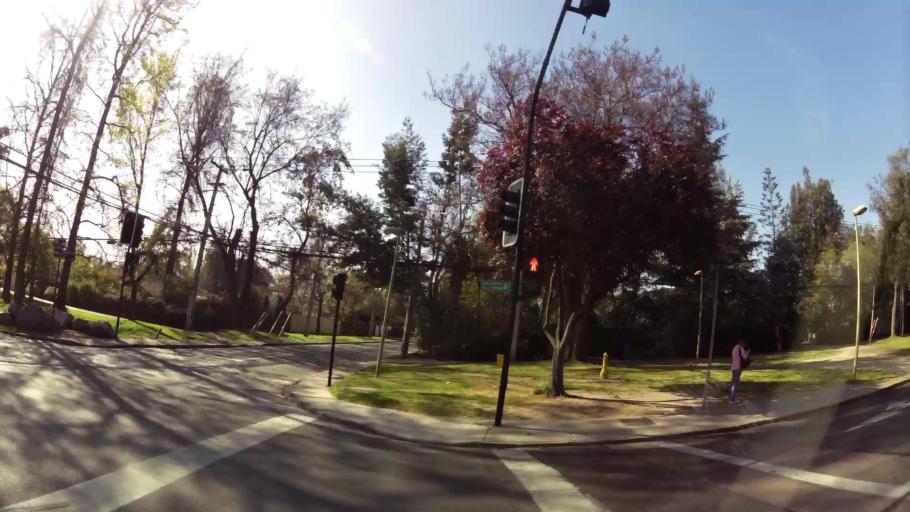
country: CL
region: Santiago Metropolitan
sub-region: Provincia de Santiago
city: Villa Presidente Frei, Nunoa, Santiago, Chile
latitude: -33.3947
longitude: -70.5250
